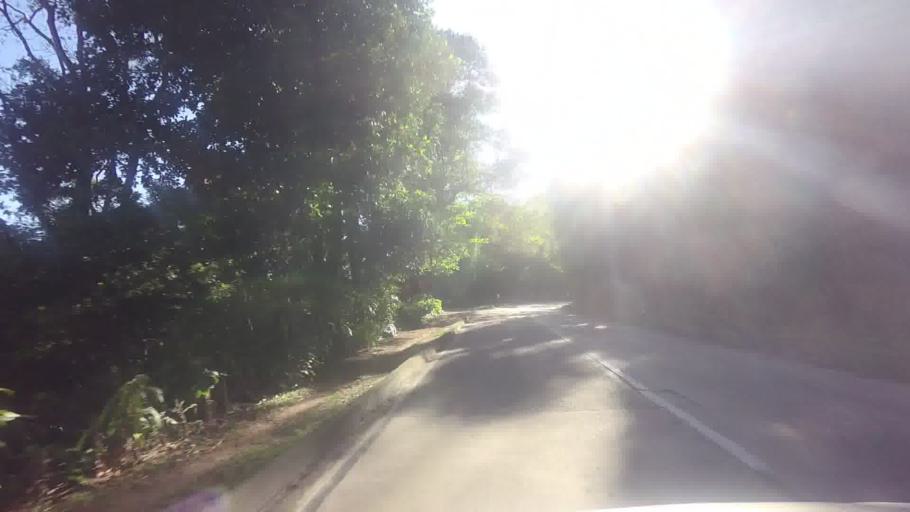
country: BR
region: Rio de Janeiro
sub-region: Petropolis
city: Petropolis
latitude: -22.5865
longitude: -43.2655
